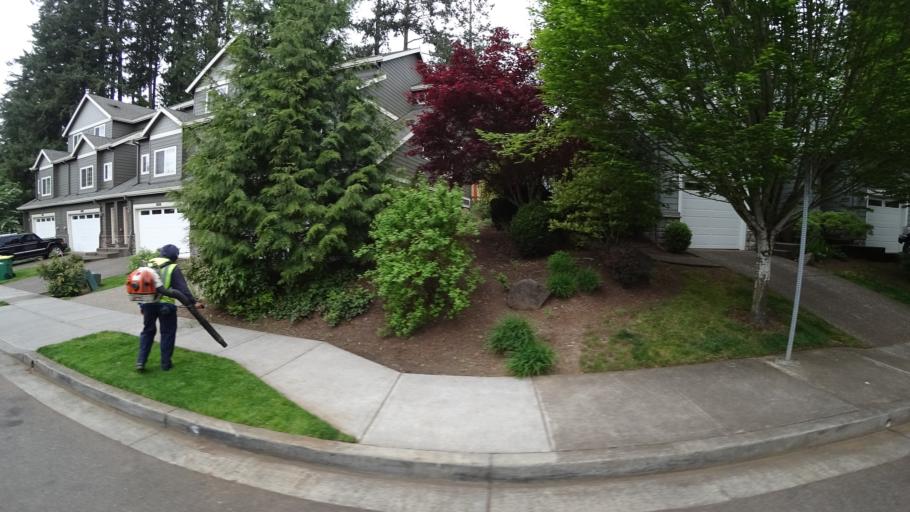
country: US
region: Oregon
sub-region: Washington County
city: Beaverton
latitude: 45.4522
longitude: -122.8333
